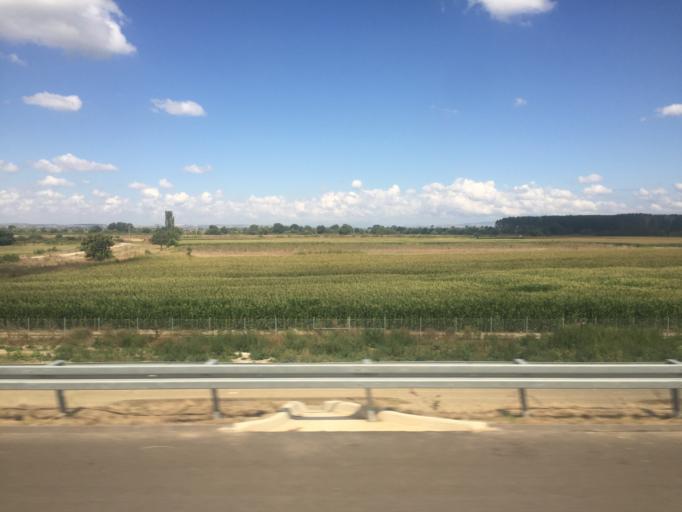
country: TR
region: Bursa
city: Karacabey
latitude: 40.1373
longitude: 28.2982
